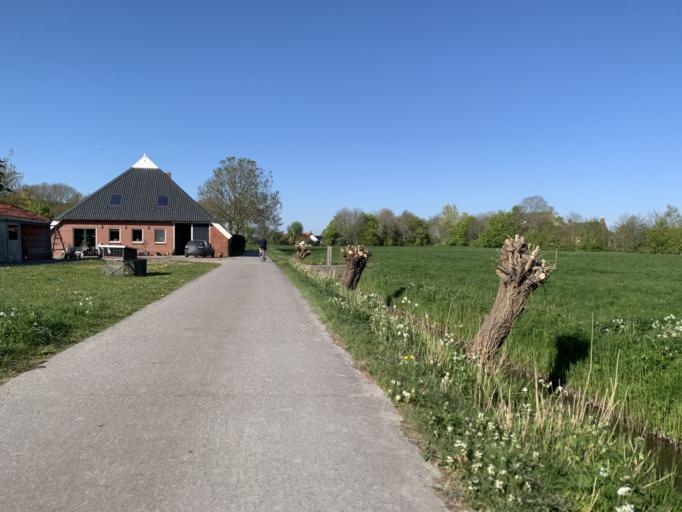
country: NL
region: Groningen
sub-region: Gemeente Winsum
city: Winsum
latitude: 53.2856
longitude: 6.5157
